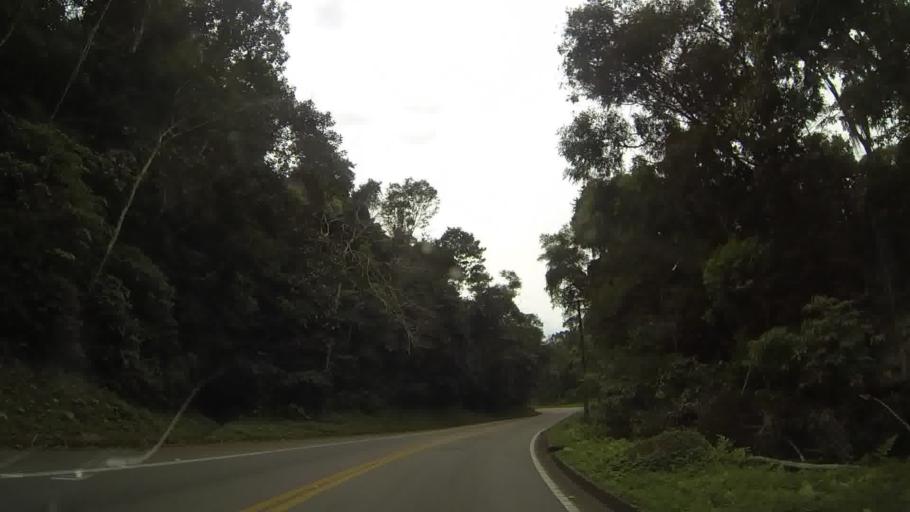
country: BR
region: Sao Paulo
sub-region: Sao Sebastiao
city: Sao Sebastiao
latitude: -23.8169
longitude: -45.4718
